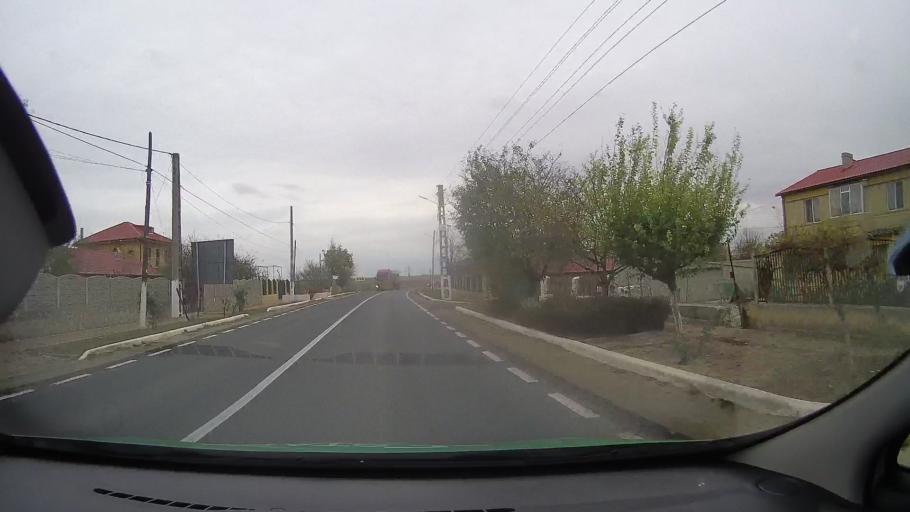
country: RO
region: Constanta
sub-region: Comuna Nicolae Balcescu
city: Nicolae Balcescu
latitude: 44.3874
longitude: 28.3857
